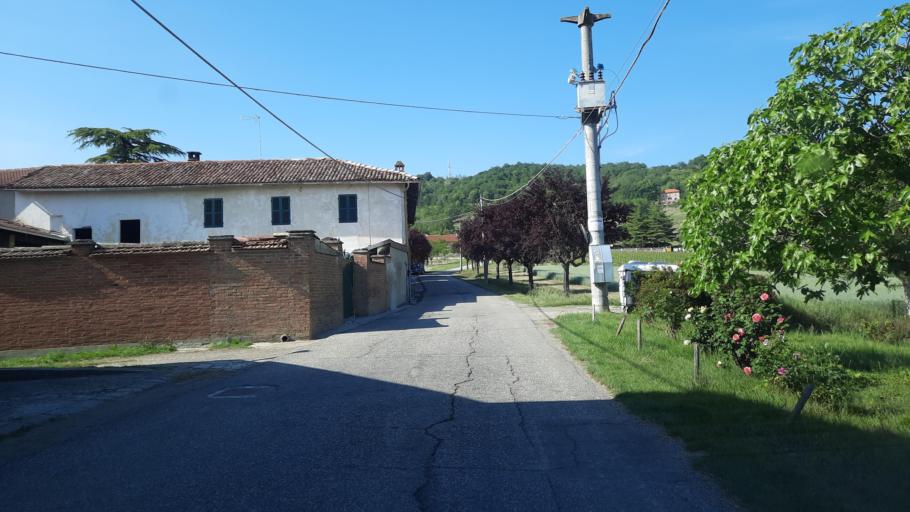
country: IT
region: Piedmont
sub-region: Provincia di Alessandria
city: Alfiano Natta
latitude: 45.0487
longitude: 8.1986
